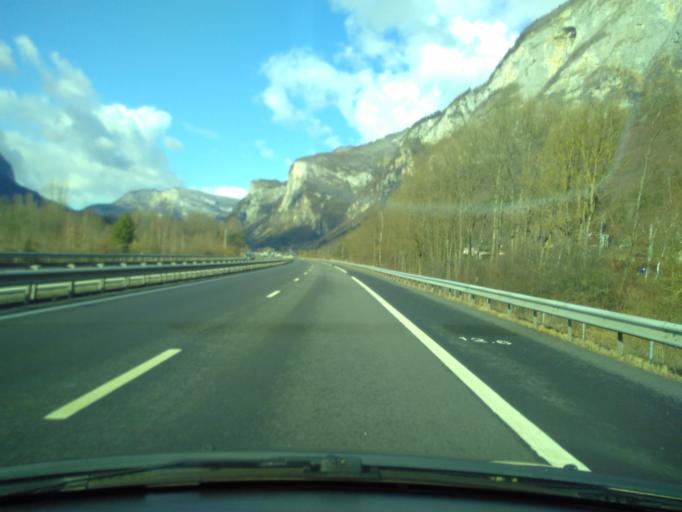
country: FR
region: Rhone-Alpes
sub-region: Departement de la Haute-Savoie
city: Magland
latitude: 45.9907
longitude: 6.6303
